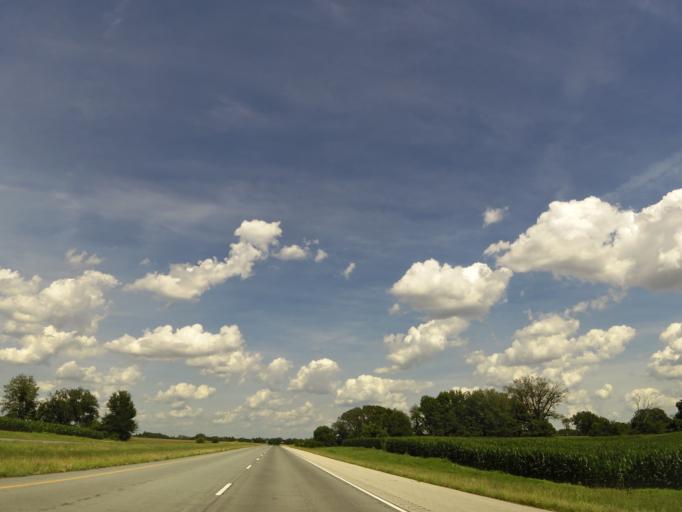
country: US
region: Tennessee
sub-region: Gibson County
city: Dyer
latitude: 35.9946
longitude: -89.0166
